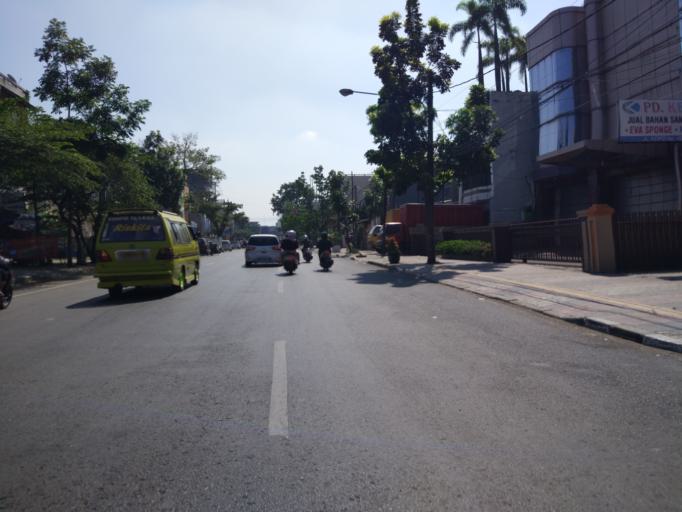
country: ID
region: West Java
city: Bandung
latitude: -6.9293
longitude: 107.5976
